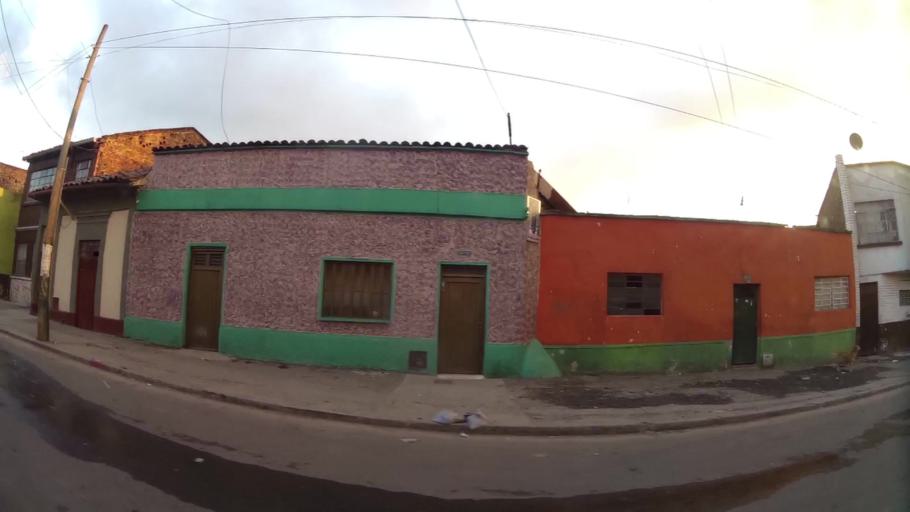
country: CO
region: Bogota D.C.
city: Bogota
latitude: 4.5883
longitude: -74.0832
